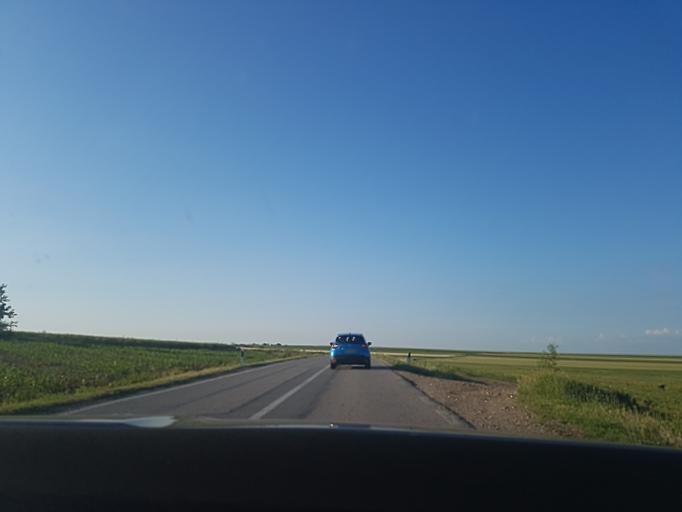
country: RS
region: Autonomna Pokrajina Vojvodina
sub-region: Juznobanatski Okrug
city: Vrsac
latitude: 45.1504
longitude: 21.2905
